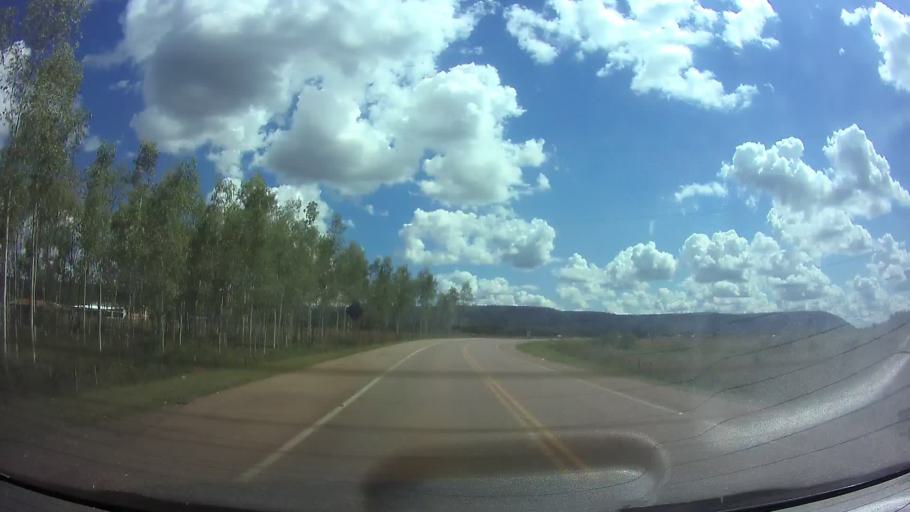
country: PY
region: Guaira
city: Itape
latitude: -25.9121
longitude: -56.6778
